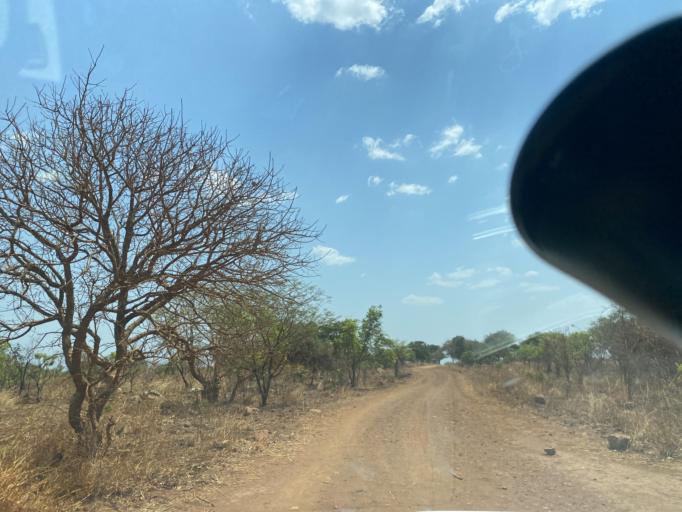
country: ZM
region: Lusaka
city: Lusaka
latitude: -15.4979
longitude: 27.9535
